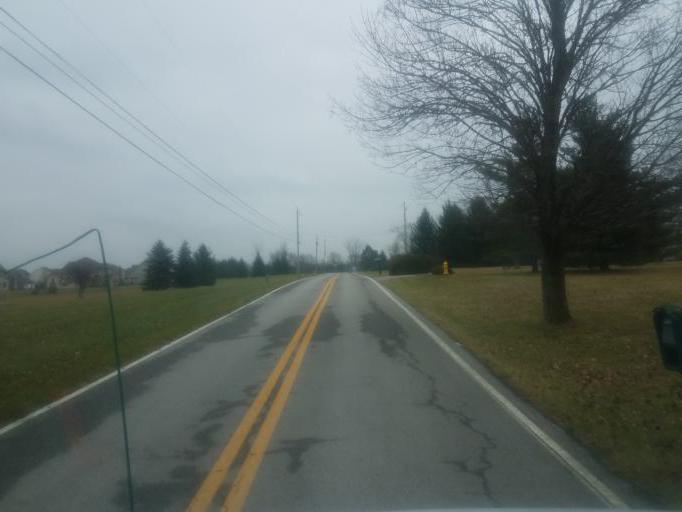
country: US
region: Ohio
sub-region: Franklin County
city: Westerville
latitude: 40.1899
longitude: -82.9241
